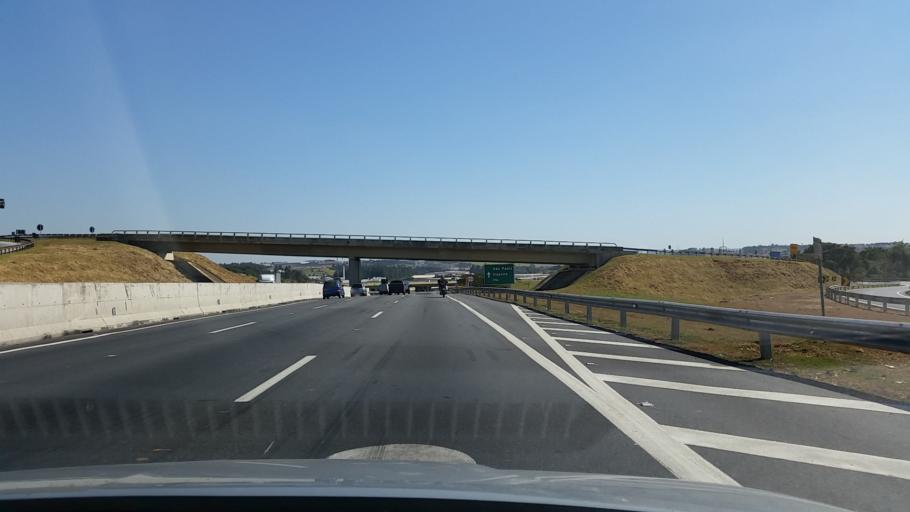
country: BR
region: Sao Paulo
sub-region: Jundiai
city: Jundiai
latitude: -23.1728
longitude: -46.9338
